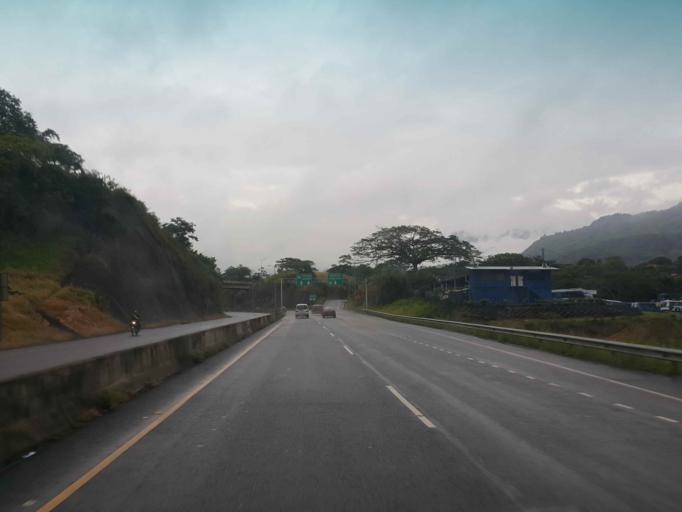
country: CR
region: Heredia
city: Colon
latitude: 9.9379
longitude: -84.2234
